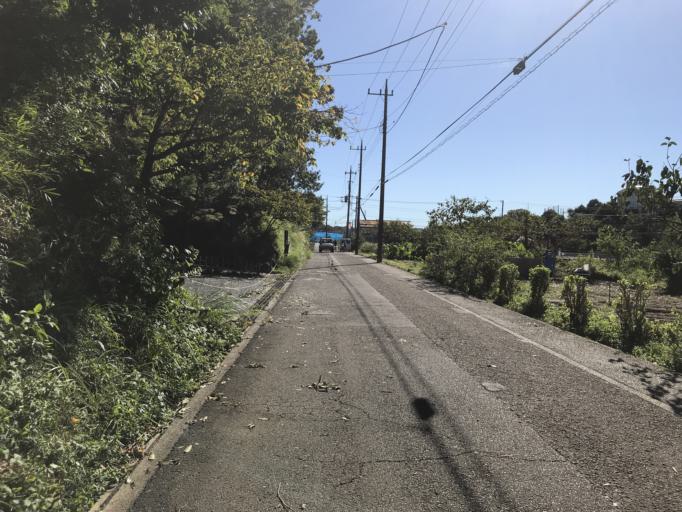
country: JP
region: Tokyo
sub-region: Machida-shi
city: Machida
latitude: 35.5680
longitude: 139.5034
